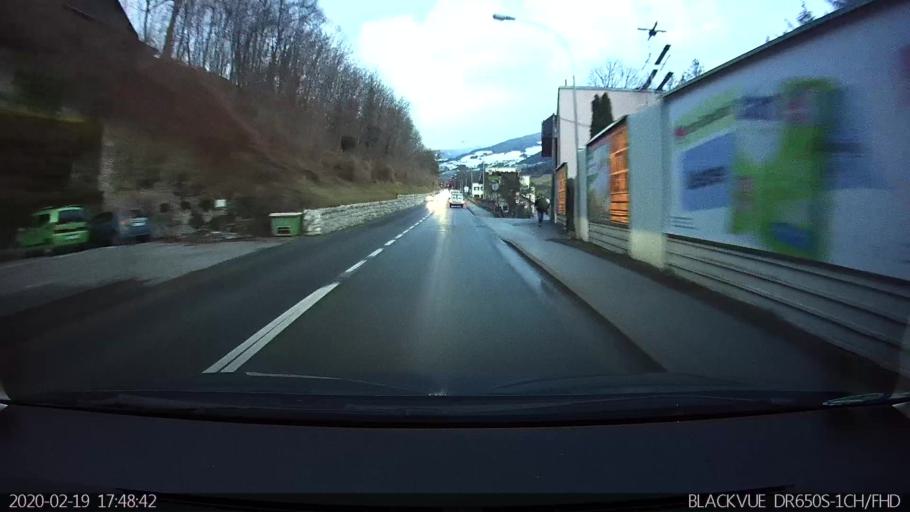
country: AT
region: Tyrol
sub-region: Politischer Bezirk Innsbruck Land
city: Hall in Tirol
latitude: 47.2807
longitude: 11.5139
